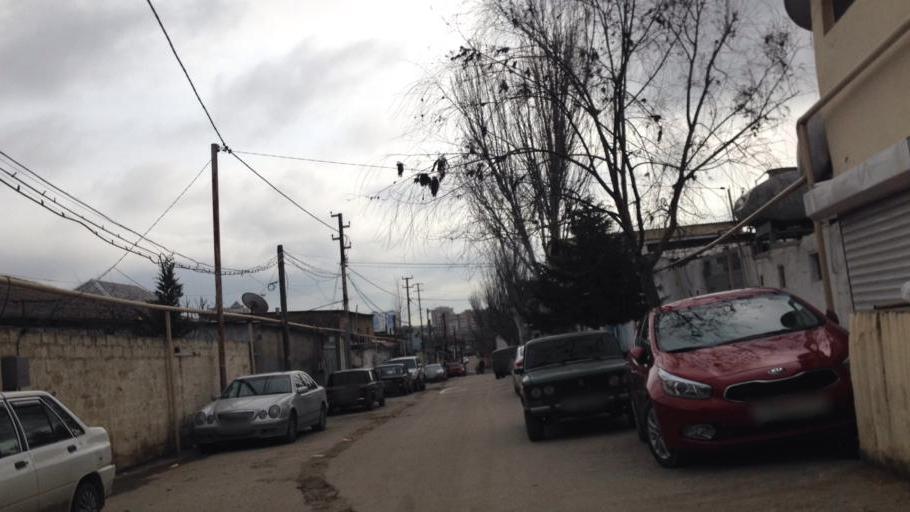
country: AZ
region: Baki
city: Bilajari
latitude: 40.4023
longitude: 49.8270
